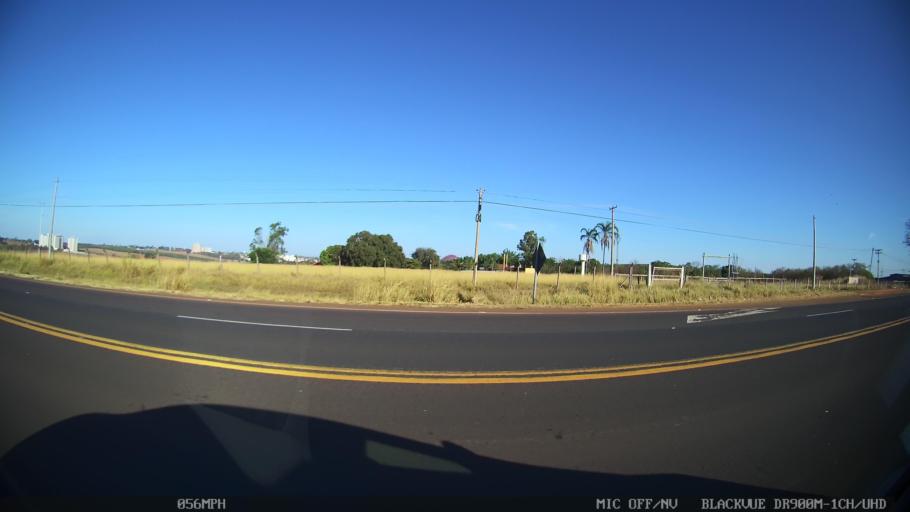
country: BR
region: Sao Paulo
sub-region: Olimpia
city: Olimpia
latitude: -20.6997
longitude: -48.9369
